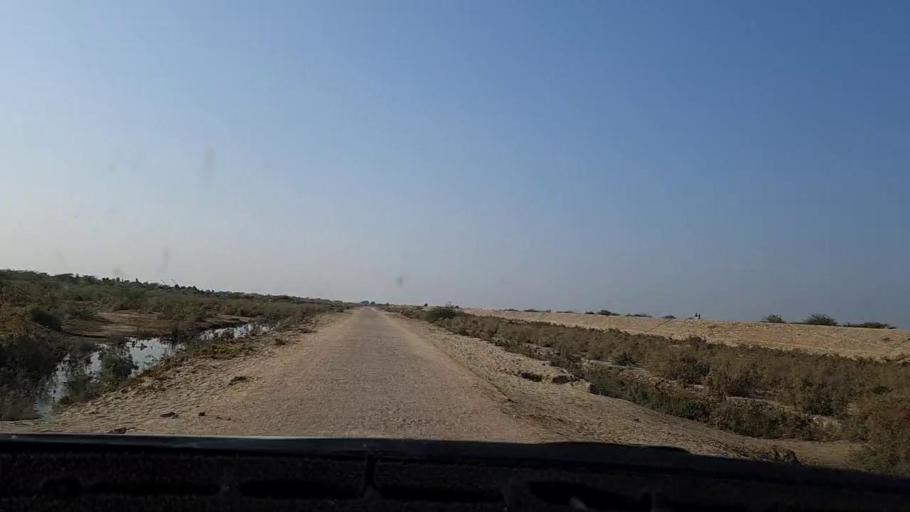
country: PK
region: Sindh
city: Tando Mittha Khan
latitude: 25.8335
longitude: 69.3157
